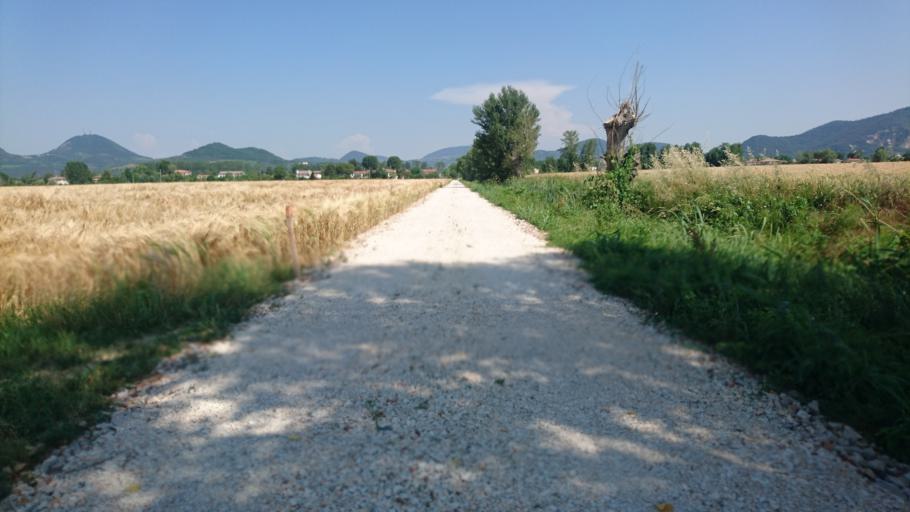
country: IT
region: Veneto
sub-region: Provincia di Padova
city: Monselice
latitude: 45.2204
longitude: 11.7236
